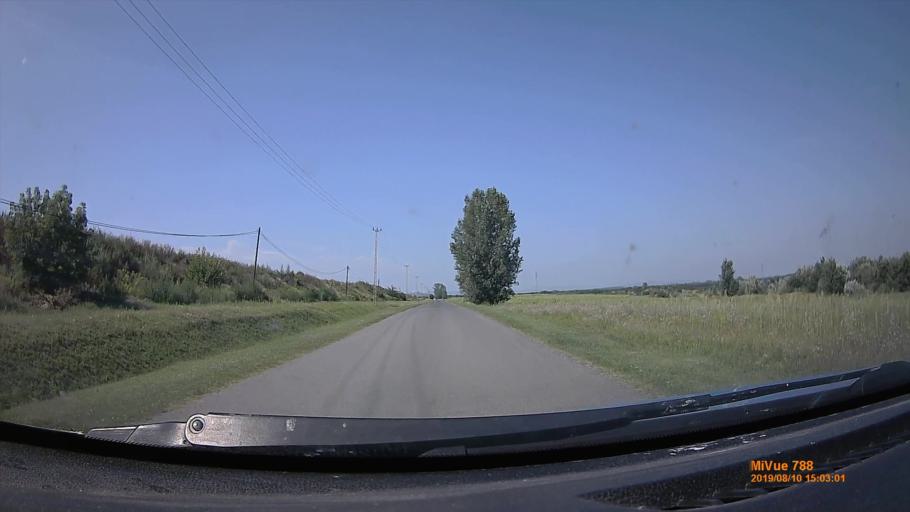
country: HU
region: Somogy
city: Lengyeltoti
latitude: 46.6609
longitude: 17.5733
